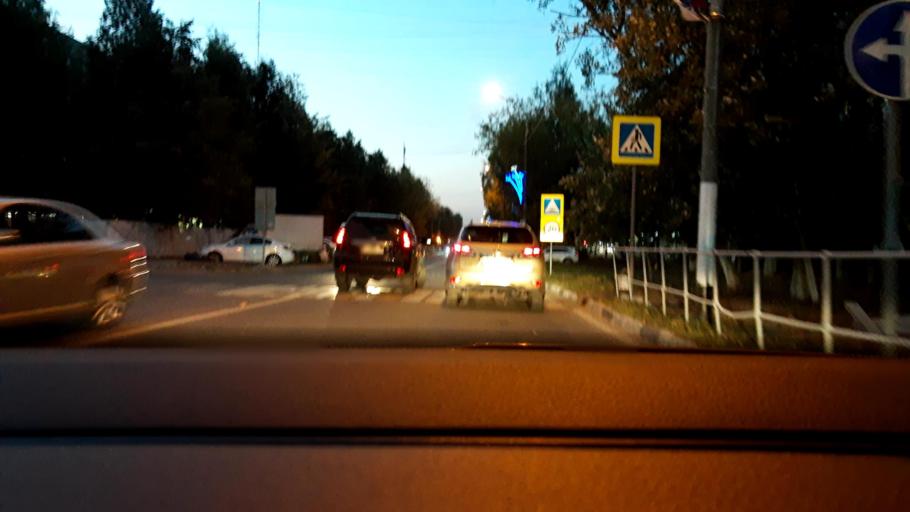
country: RU
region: Moskovskaya
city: Dolgoprudnyy
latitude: 55.9397
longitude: 37.5102
